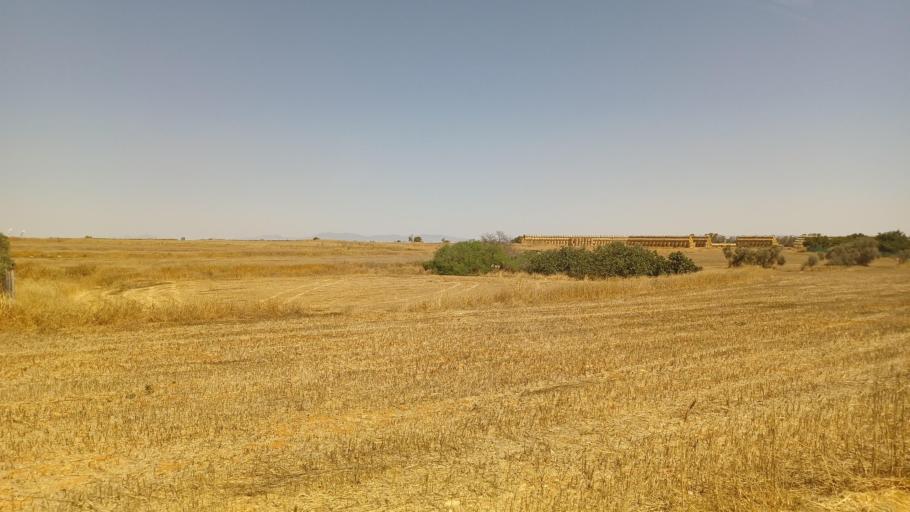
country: CY
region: Larnaka
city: Xylotymbou
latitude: 35.0147
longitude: 33.7271
